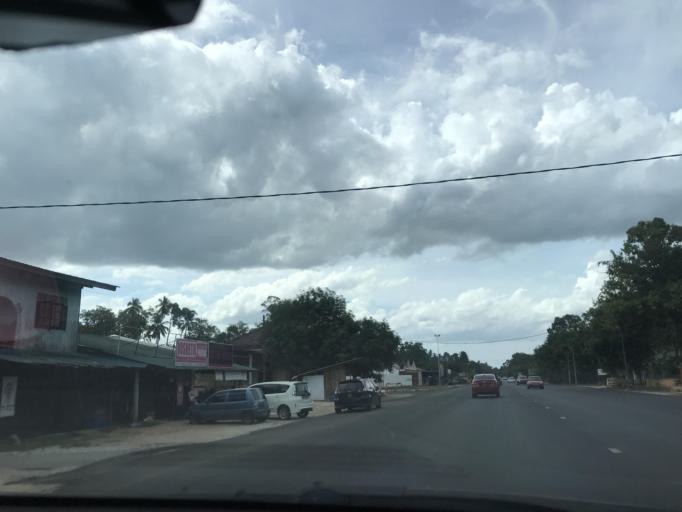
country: MY
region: Kelantan
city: Kampong Pangkal Kalong
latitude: 5.9268
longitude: 102.1902
